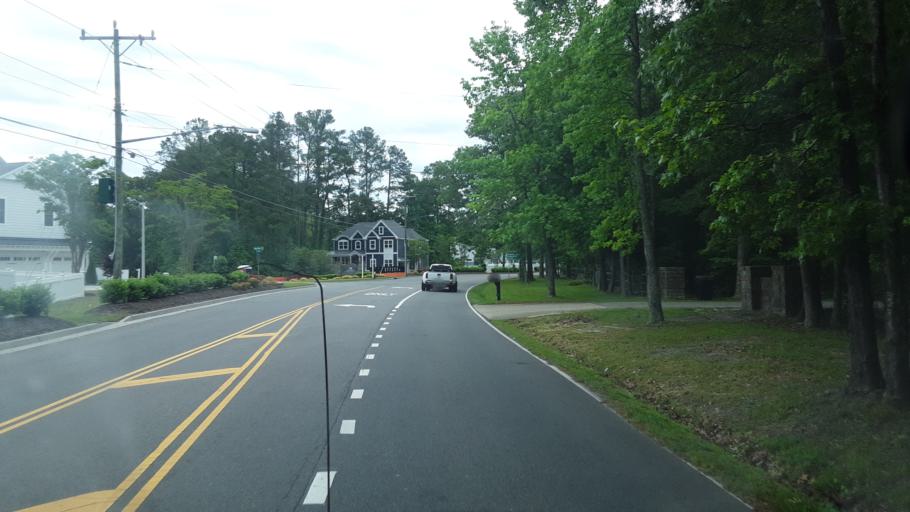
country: US
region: Virginia
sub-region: City of Virginia Beach
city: Virginia Beach
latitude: 36.7421
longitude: -75.9892
